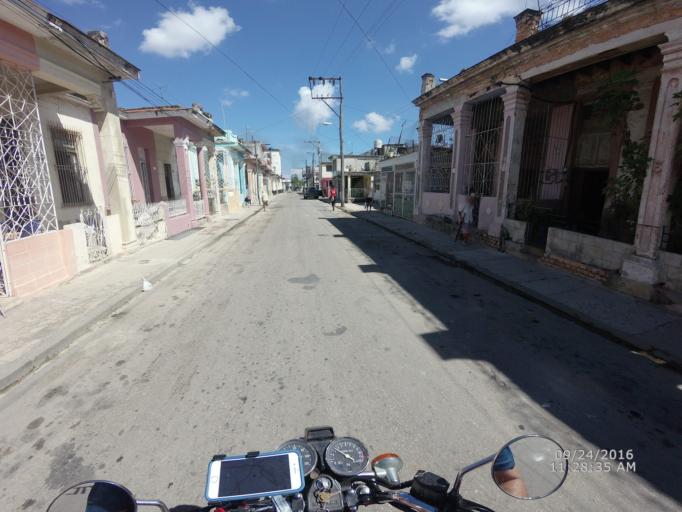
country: CU
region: La Habana
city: Cerro
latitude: 23.1124
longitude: -82.3647
